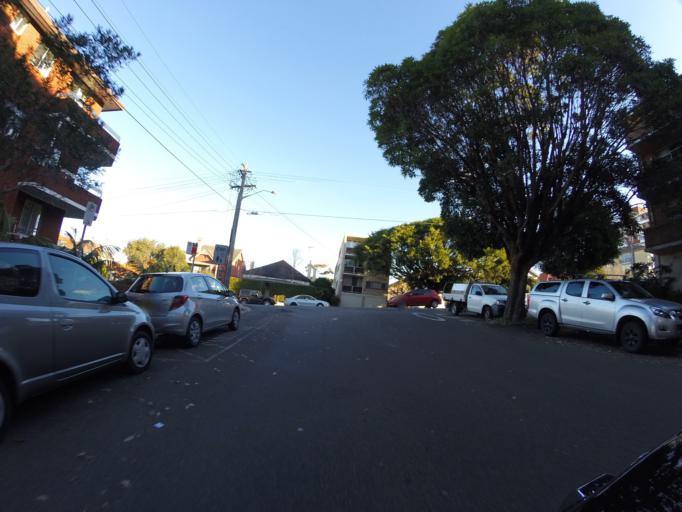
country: AU
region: New South Wales
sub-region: Waverley
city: Bondi
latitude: -33.8972
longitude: 151.2618
